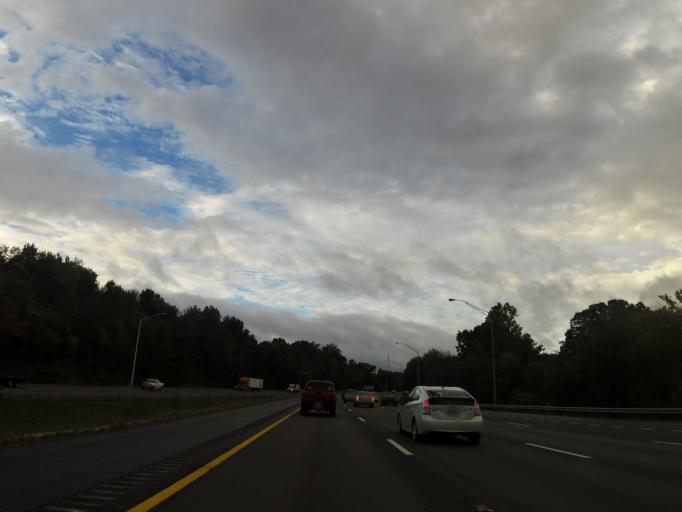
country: US
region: Tennessee
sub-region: Knox County
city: Knoxville
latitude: 35.9790
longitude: -83.9792
